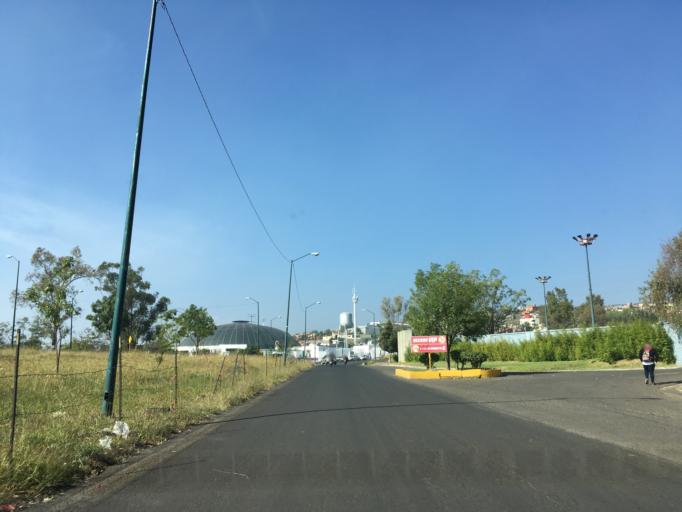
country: MX
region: Michoacan
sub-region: Tarimbaro
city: Fraccionamiento Metropolis II
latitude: 19.7168
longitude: -101.2311
